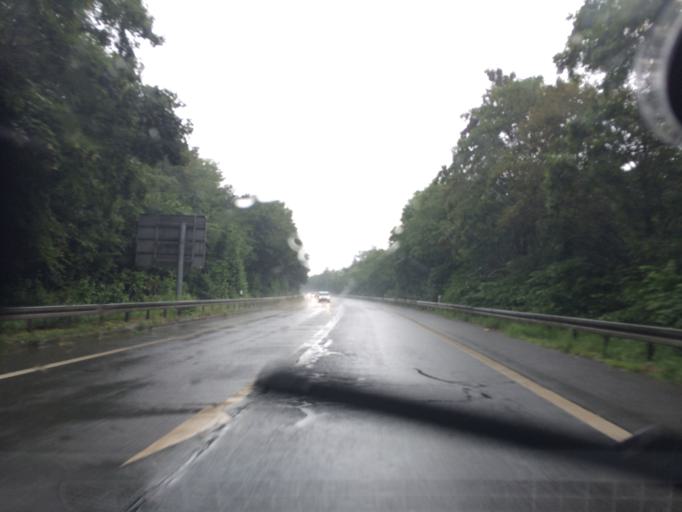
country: DE
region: North Rhine-Westphalia
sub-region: Regierungsbezirk Munster
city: Haltern
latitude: 51.7668
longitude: 7.2358
